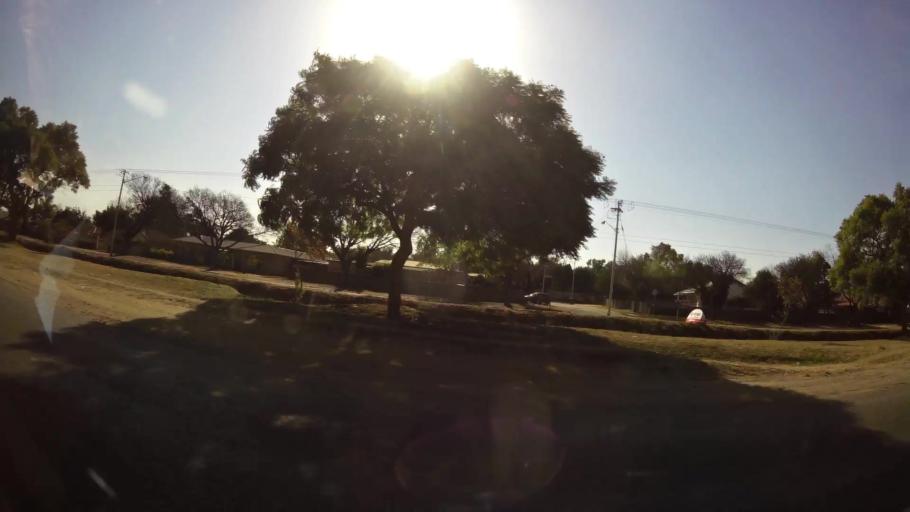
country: ZA
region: Gauteng
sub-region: City of Tshwane Metropolitan Municipality
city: Pretoria
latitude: -25.7166
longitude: 28.2471
